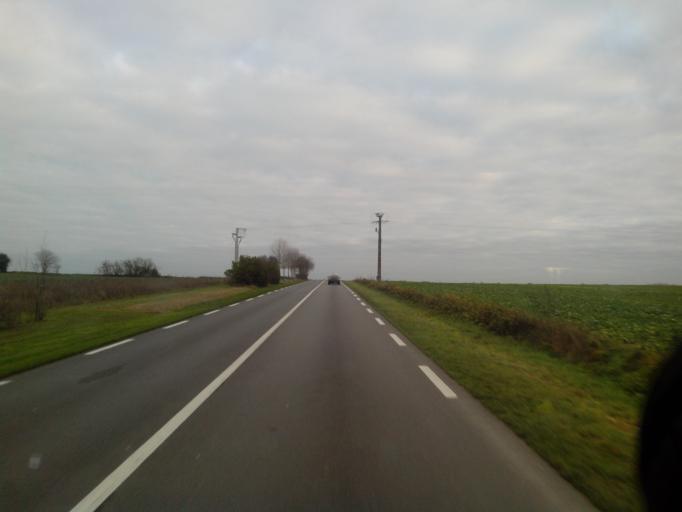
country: FR
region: Poitou-Charentes
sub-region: Departement de la Vienne
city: Vouille
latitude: 46.6447
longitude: 0.1846
